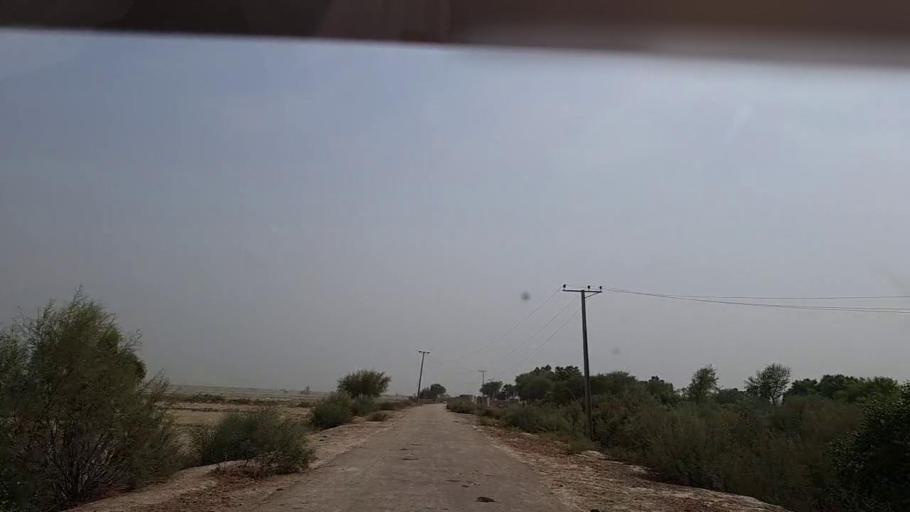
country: PK
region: Sindh
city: Khairpur Nathan Shah
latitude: 27.0416
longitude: 67.6862
